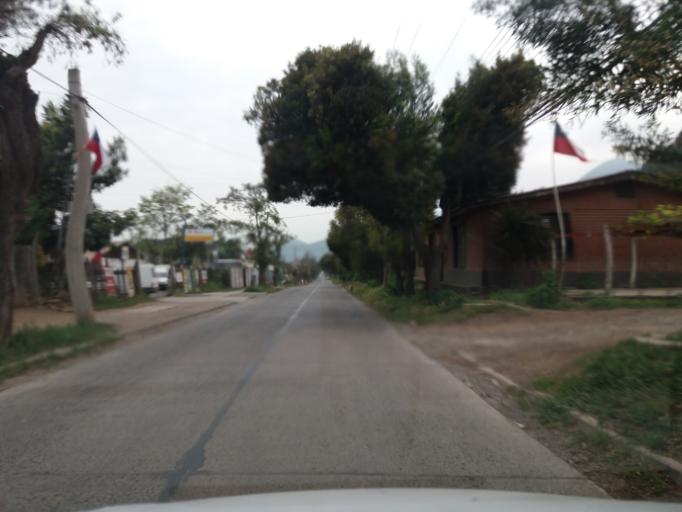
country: CL
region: Valparaiso
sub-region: Provincia de Quillota
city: Hacienda La Calera
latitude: -32.8109
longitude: -71.1411
